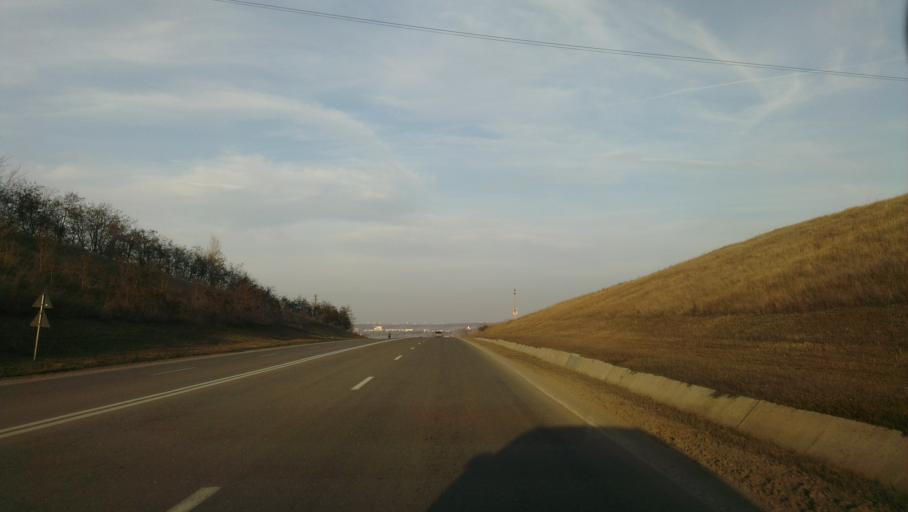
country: MD
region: Laloveni
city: Ialoveni
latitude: 46.9438
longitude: 28.7088
